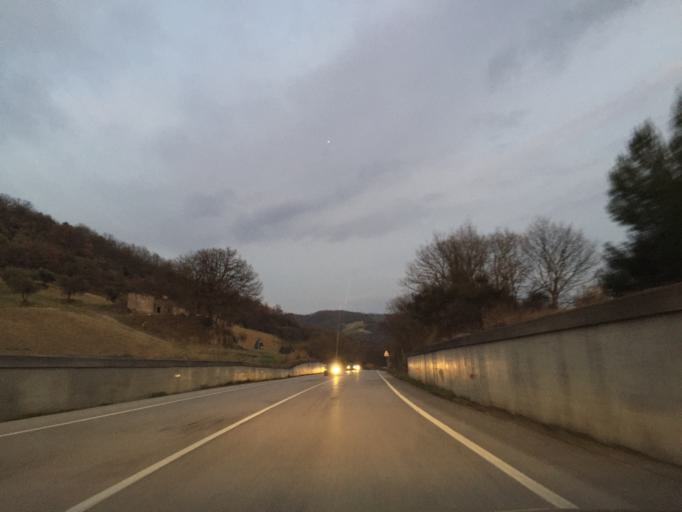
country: IT
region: Apulia
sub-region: Provincia di Foggia
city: San Marco la Catola
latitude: 41.5040
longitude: 15.0093
